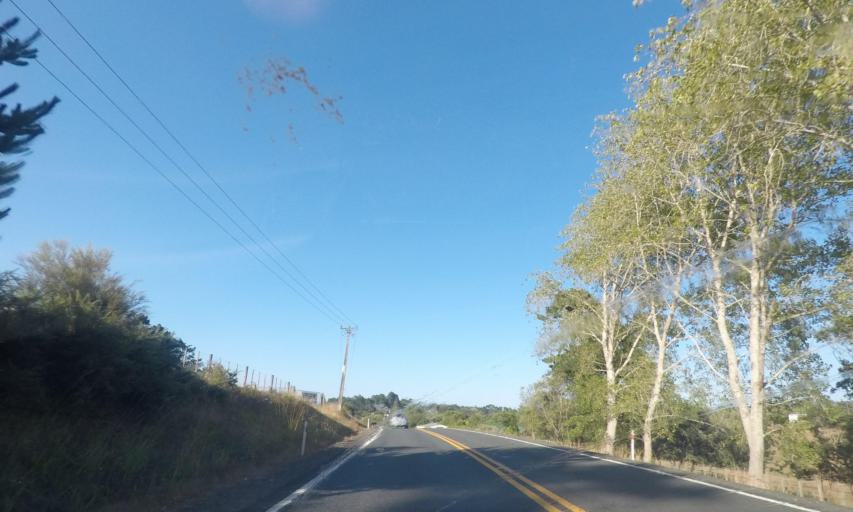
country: NZ
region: Auckland
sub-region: Auckland
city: Muriwai Beach
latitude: -36.7771
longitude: 174.4851
